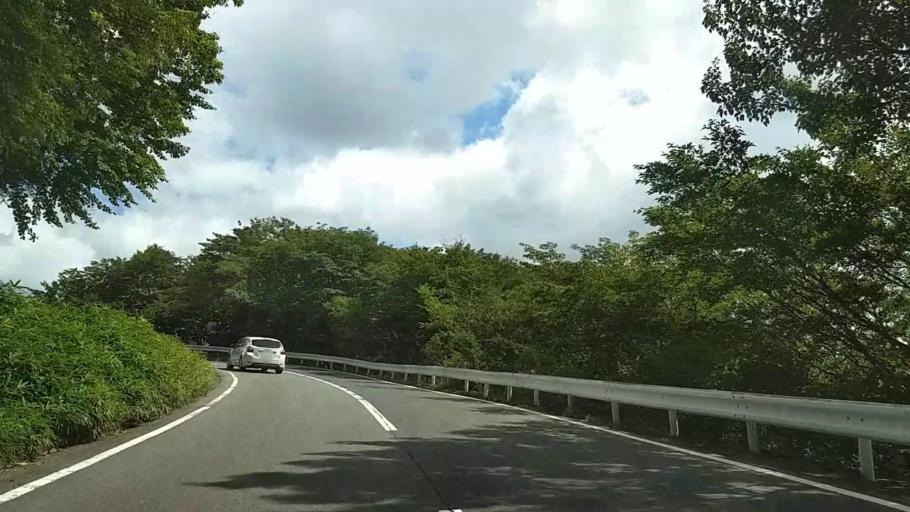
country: JP
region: Tochigi
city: Nikko
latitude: 36.7311
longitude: 139.5178
